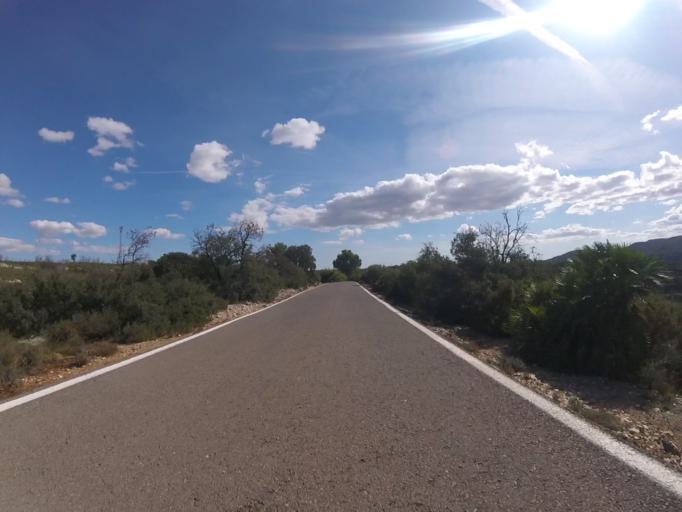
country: ES
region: Valencia
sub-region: Provincia de Castello
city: Albocasser
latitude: 40.3968
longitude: 0.0893
